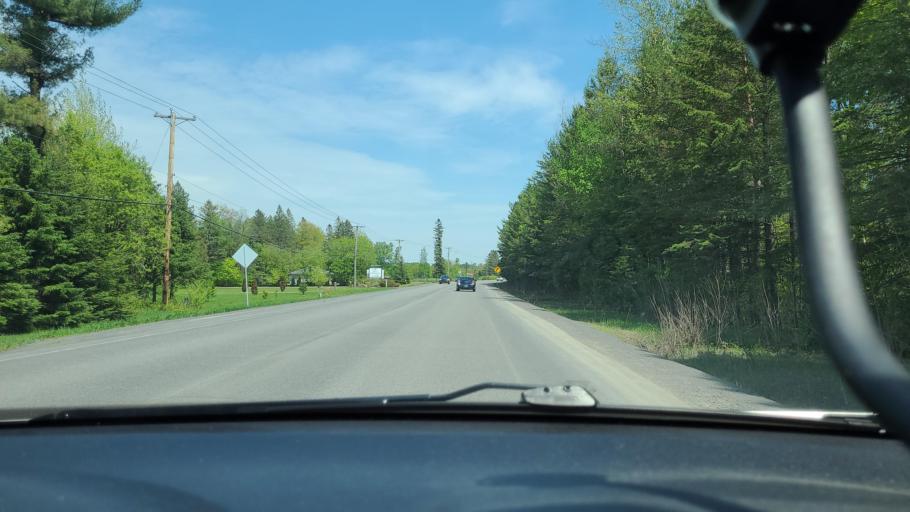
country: CA
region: Quebec
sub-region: Laurentides
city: Lachute
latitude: 45.6677
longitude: -74.2387
